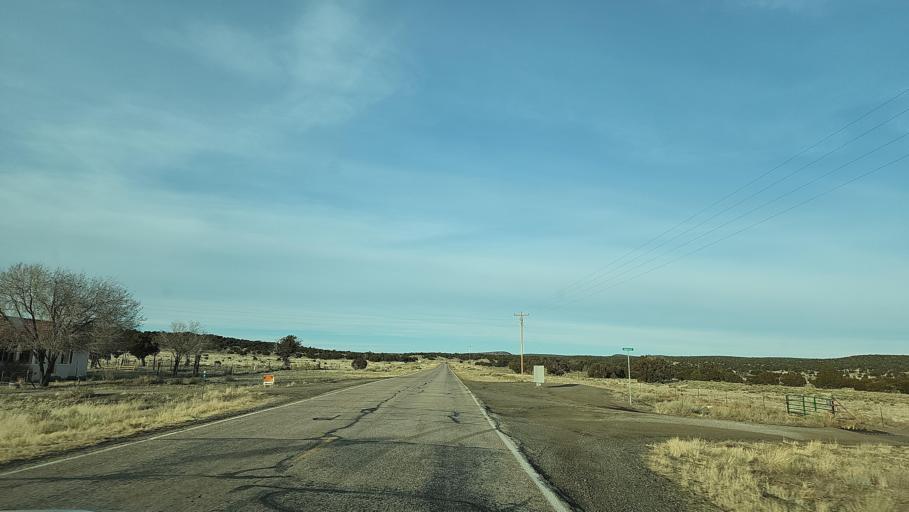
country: US
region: New Mexico
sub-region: Catron County
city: Reserve
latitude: 34.3999
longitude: -108.4422
